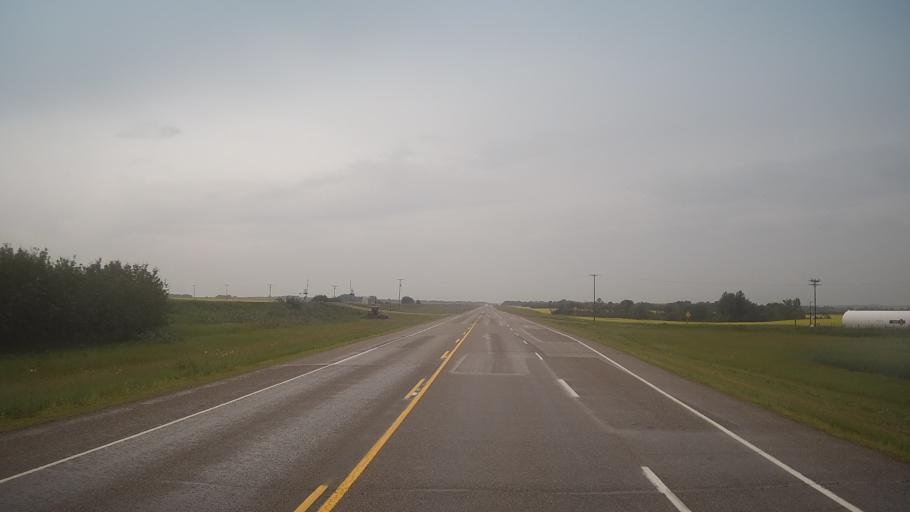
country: CA
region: Saskatchewan
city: Wilkie
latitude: 52.2300
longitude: -108.5388
